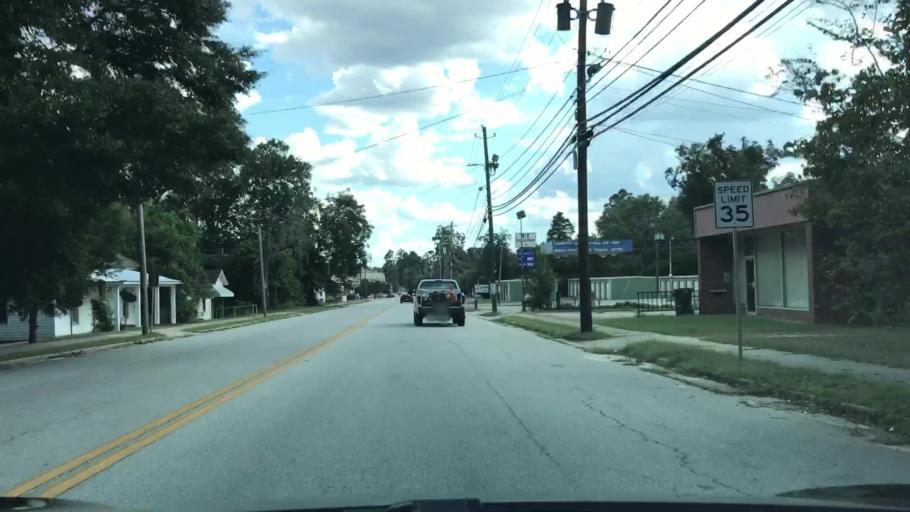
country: US
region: Georgia
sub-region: Jefferson County
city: Wadley
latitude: 32.8655
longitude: -82.4047
